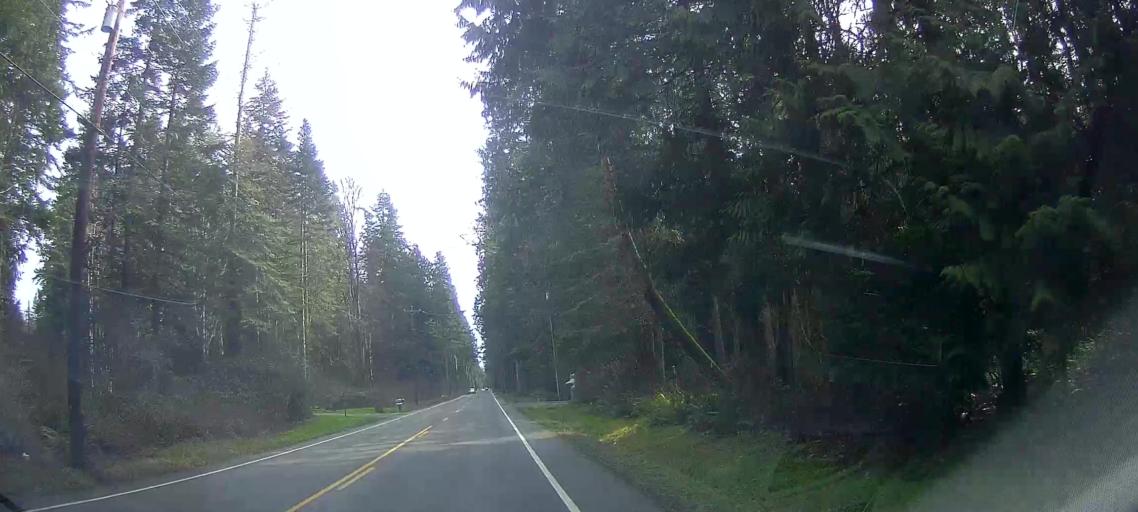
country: US
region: Washington
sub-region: Island County
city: Camano
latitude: 48.1278
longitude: -122.4598
